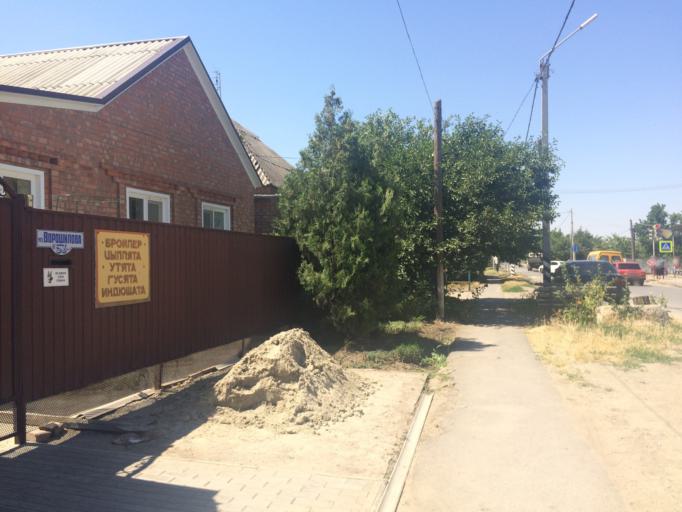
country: RU
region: Rostov
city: Sal'sk
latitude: 46.4692
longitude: 41.5367
